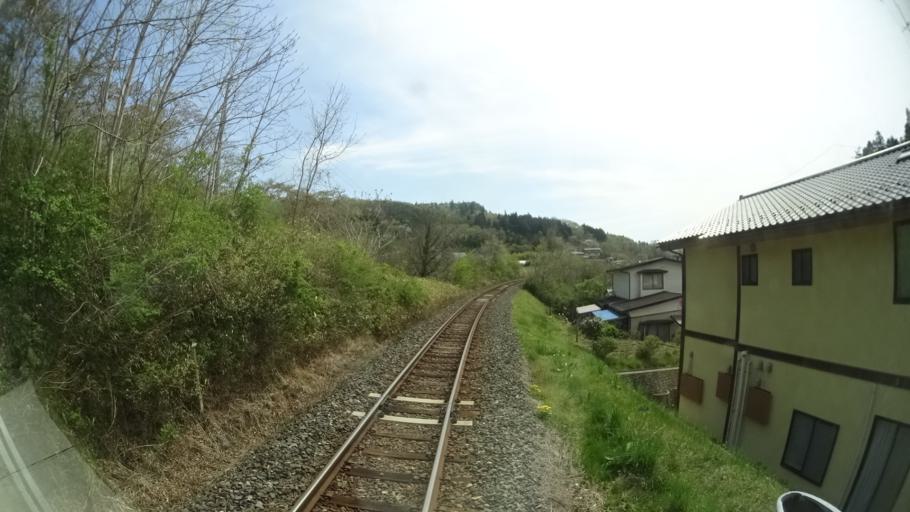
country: JP
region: Iwate
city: Ichinoseki
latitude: 39.0020
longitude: 141.2652
